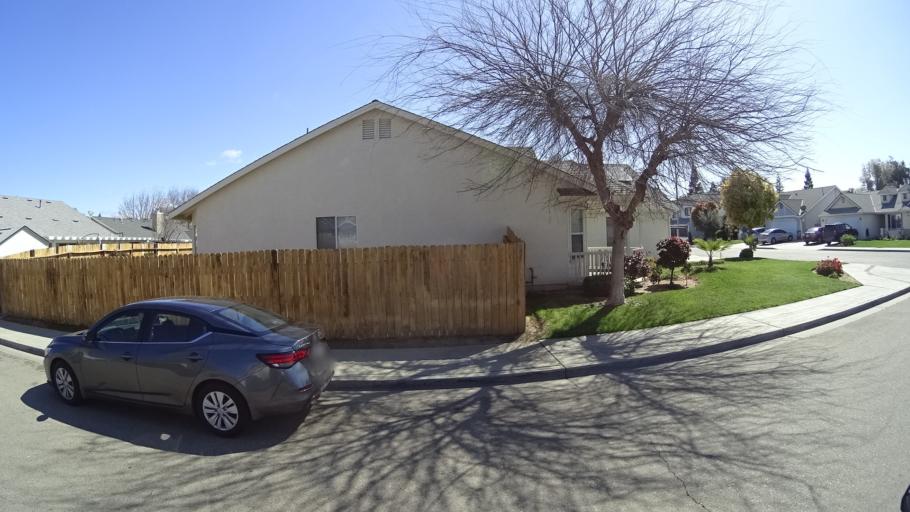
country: US
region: California
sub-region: Fresno County
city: West Park
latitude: 36.7892
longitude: -119.8887
